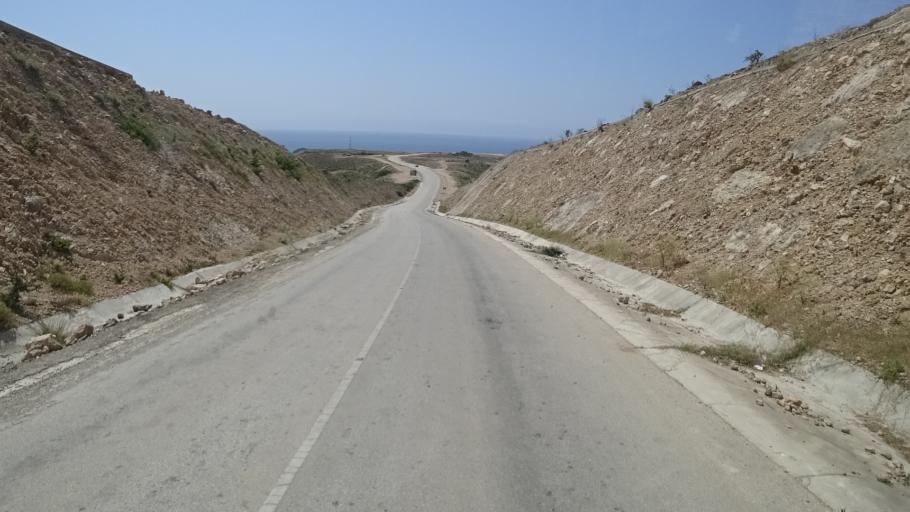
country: OM
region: Zufar
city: Salalah
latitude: 17.0448
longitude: 54.6128
